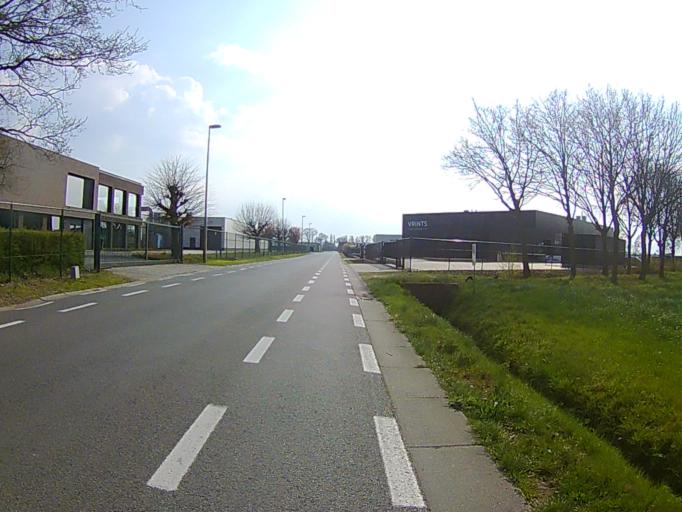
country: BE
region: Flanders
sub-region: Provincie Antwerpen
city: Essen
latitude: 51.4495
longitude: 4.4973
